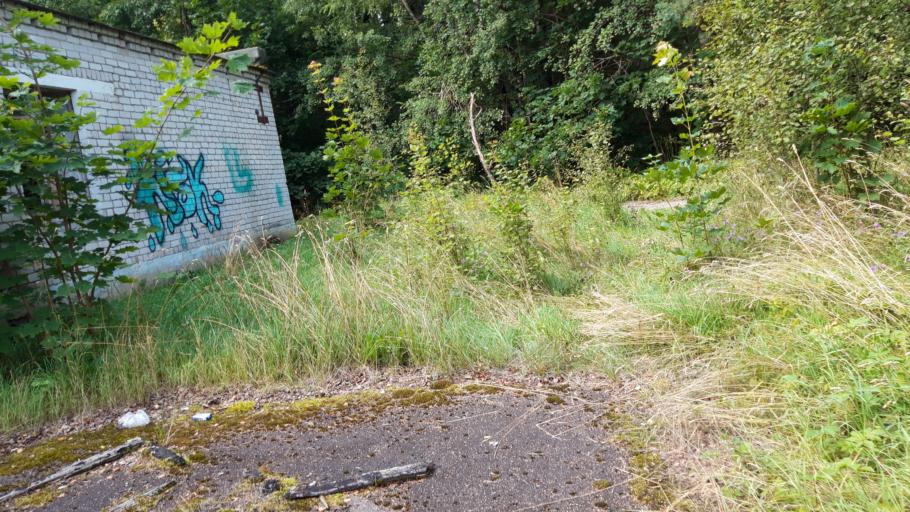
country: RU
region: Tverskaya
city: Konakovo
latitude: 56.6672
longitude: 36.6824
